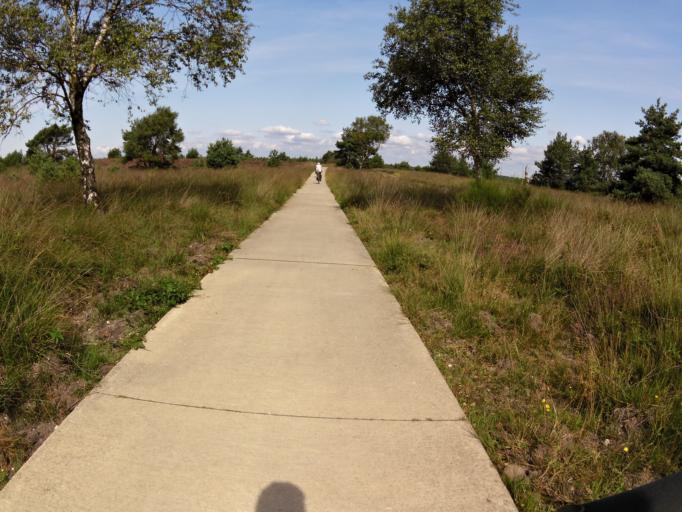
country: NL
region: Gelderland
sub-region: Gemeente Rozendaal
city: Rozendaal
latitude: 52.0425
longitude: 5.9868
